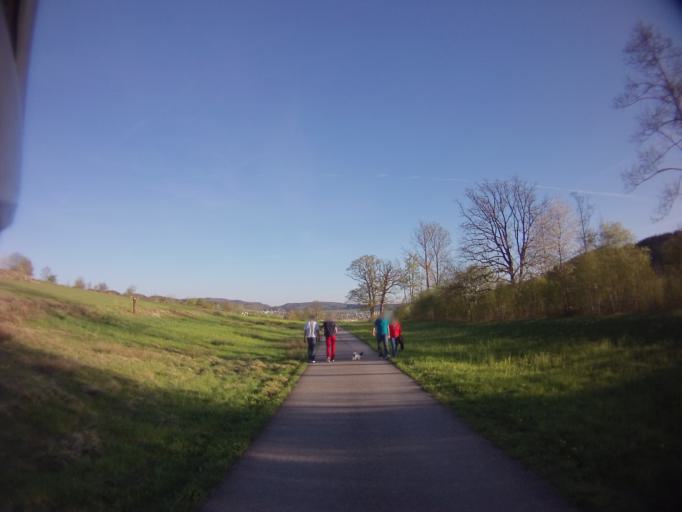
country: CH
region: Zurich
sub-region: Bezirk Affoltern
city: Wettswil / Wettswil (Dorf)
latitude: 47.3425
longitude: 8.4627
